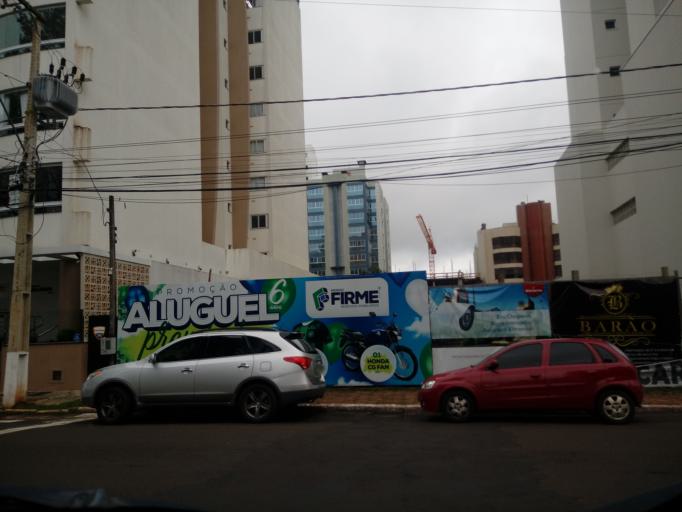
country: BR
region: Santa Catarina
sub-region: Chapeco
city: Chapeco
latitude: -27.1020
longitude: -52.6100
